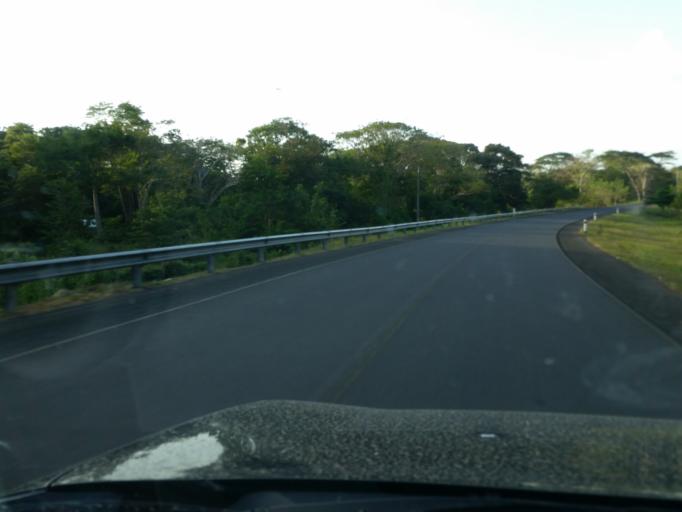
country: NI
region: Rio San Juan
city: San Carlos
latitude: 11.2628
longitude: -84.7132
